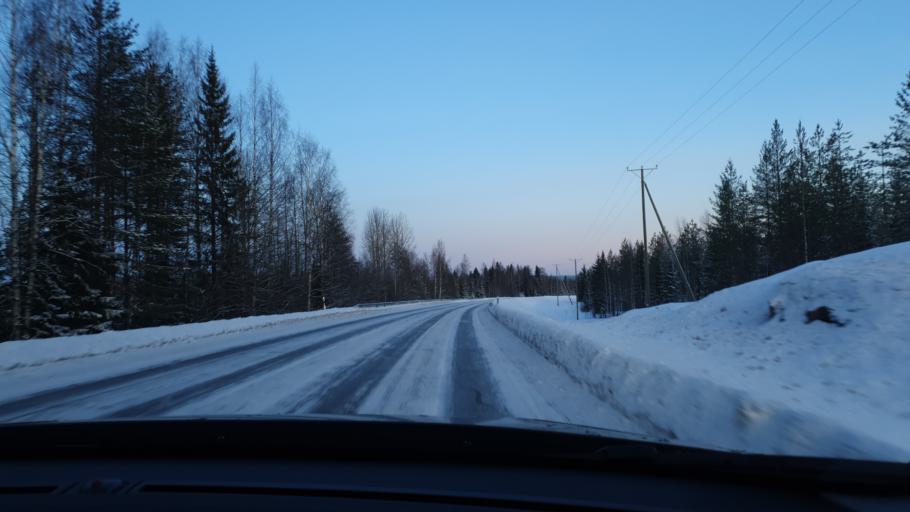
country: FI
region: Kainuu
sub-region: Kajaani
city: Sotkamo
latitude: 64.0871
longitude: 28.7193
